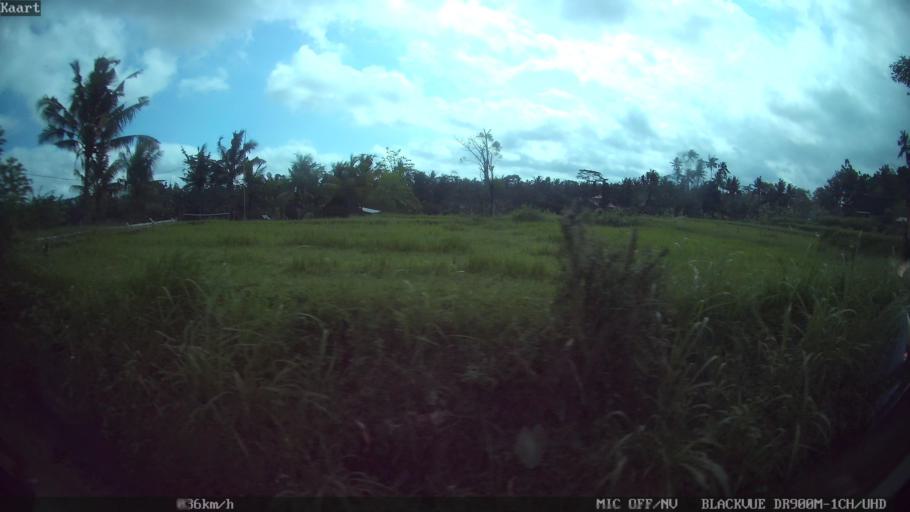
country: ID
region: Bali
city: Banjar Pesalakan
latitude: -8.4977
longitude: 115.3044
